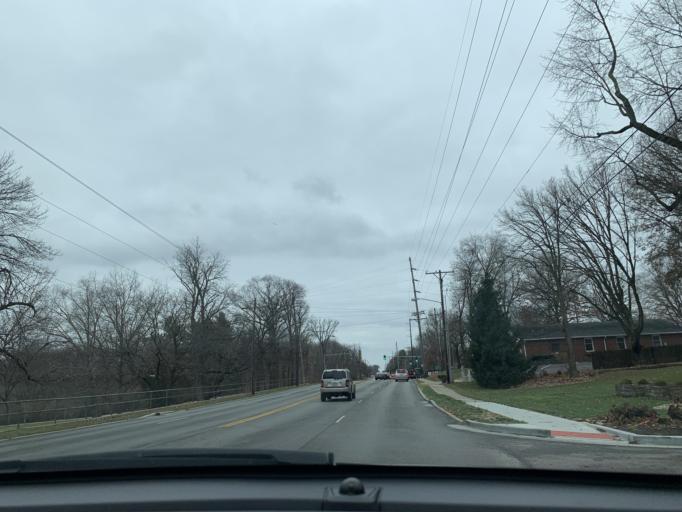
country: US
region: Illinois
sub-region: Sangamon County
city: Leland Grove
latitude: 39.7898
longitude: -89.6871
